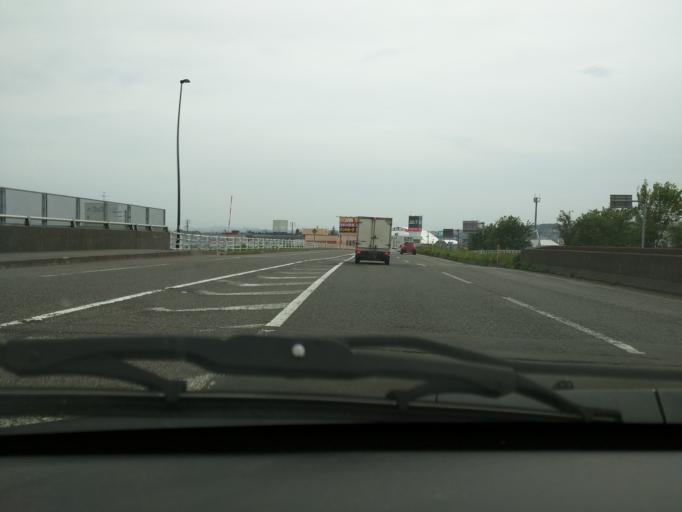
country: JP
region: Niigata
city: Nagaoka
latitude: 37.4495
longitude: 138.8002
